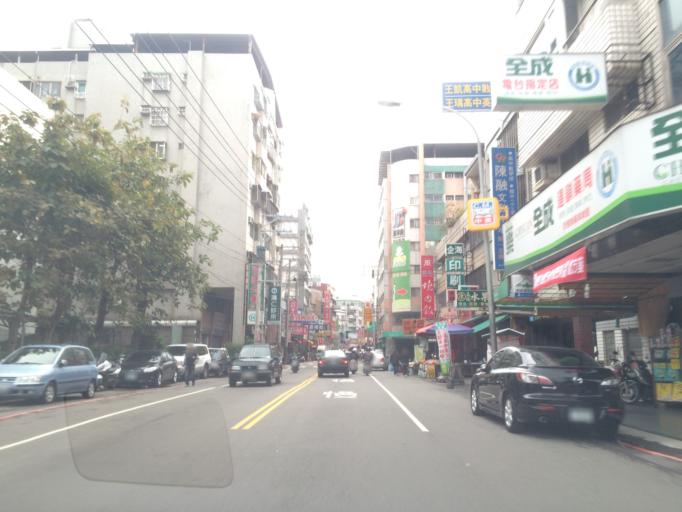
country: TW
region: Taiwan
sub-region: Taichung City
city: Taichung
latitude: 24.1789
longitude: 120.6407
